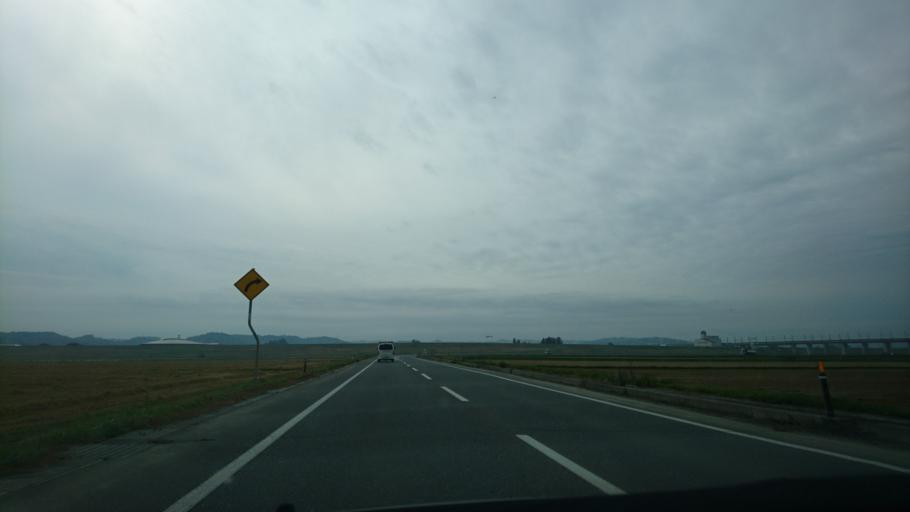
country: JP
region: Iwate
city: Ichinoseki
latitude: 38.9489
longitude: 141.1547
